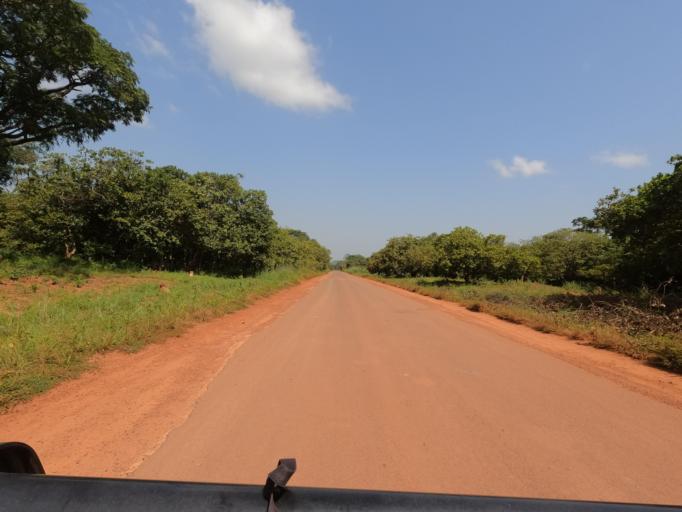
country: GW
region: Oio
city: Bissora
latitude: 12.3214
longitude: -15.7586
